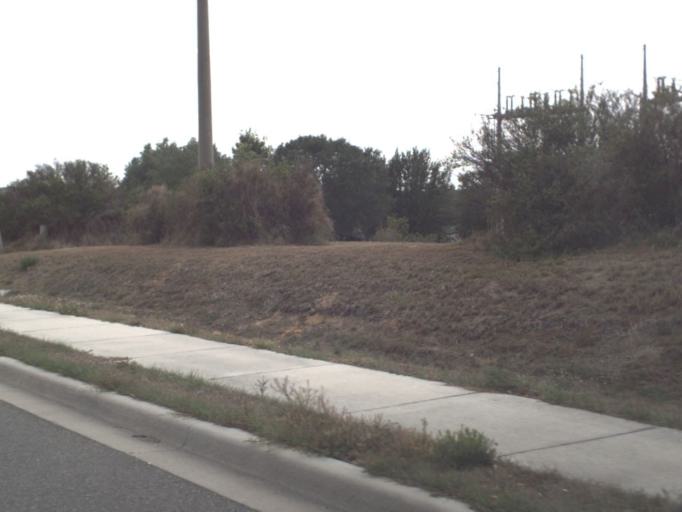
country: US
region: Florida
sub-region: Orange County
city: Oakland
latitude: 28.5466
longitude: -81.6855
